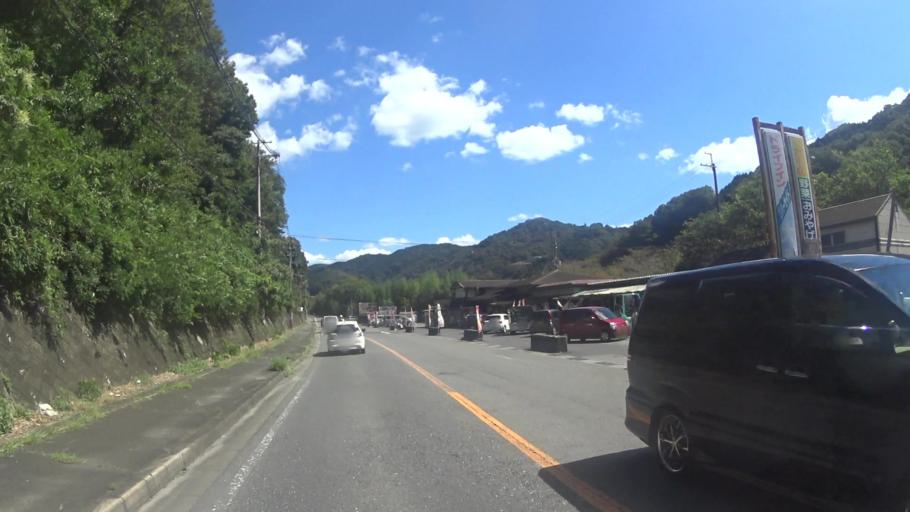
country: JP
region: Nara
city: Nara-shi
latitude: 34.7623
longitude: 135.9273
